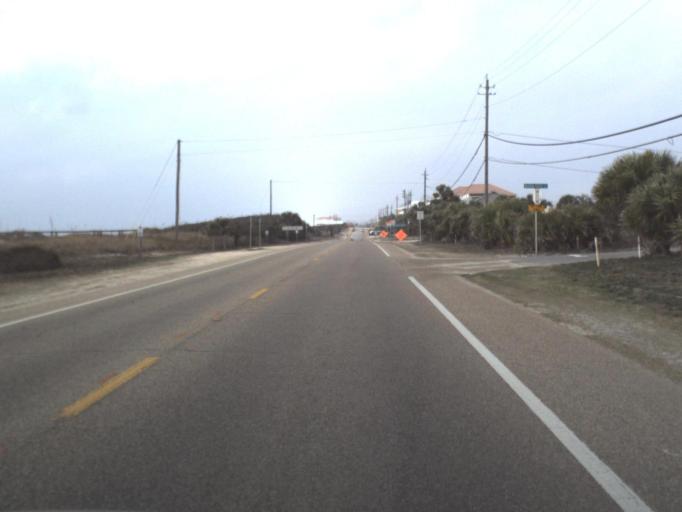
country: US
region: Florida
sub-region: Bay County
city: Laguna Beach
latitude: 30.2484
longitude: -85.9440
